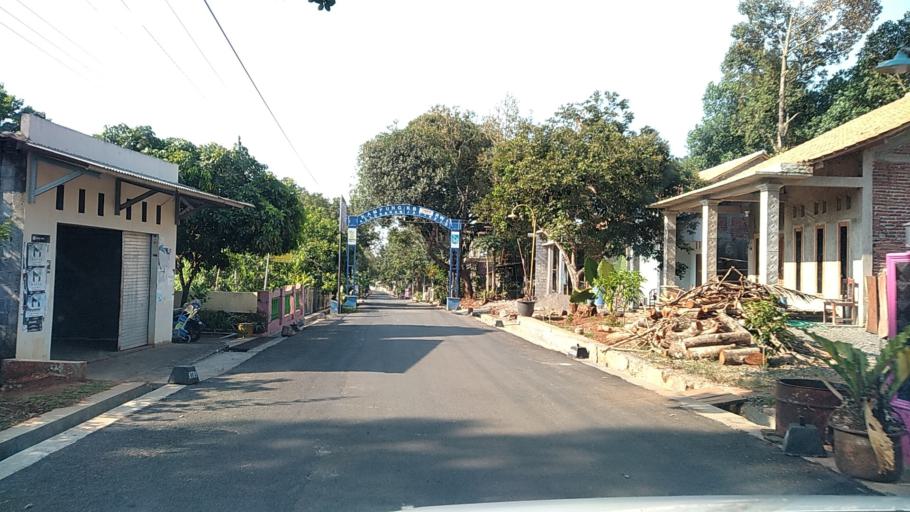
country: ID
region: Central Java
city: Ungaran
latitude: -7.0635
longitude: 110.3480
